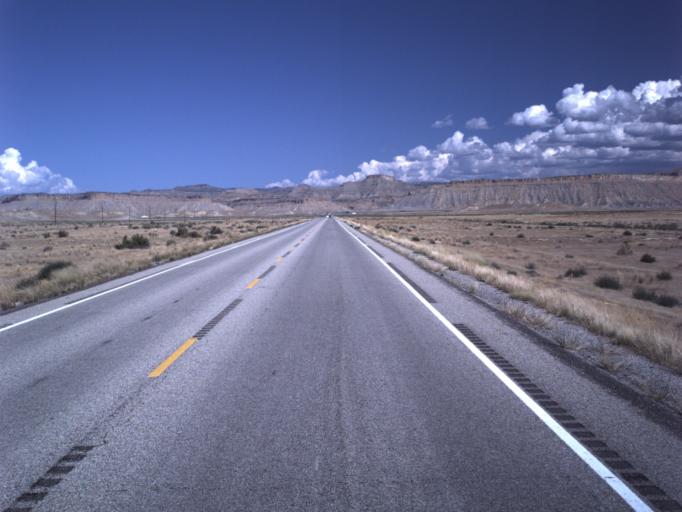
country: US
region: Utah
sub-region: Grand County
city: Moab
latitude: 38.9132
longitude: -109.8148
